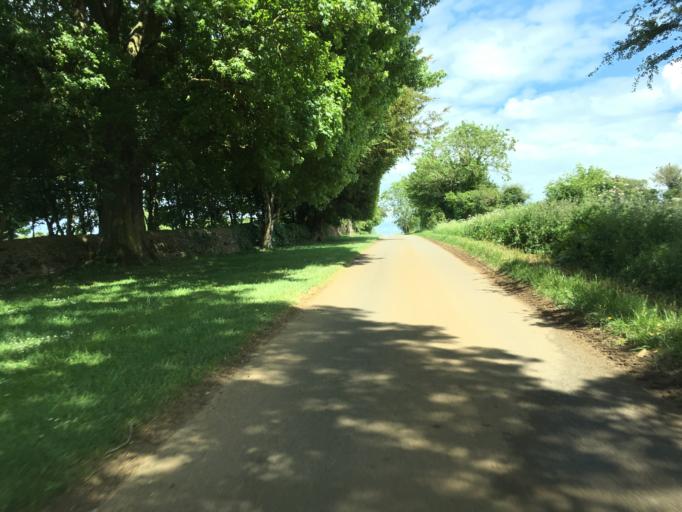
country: GB
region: England
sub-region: Gloucestershire
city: Coates
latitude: 51.6782
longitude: -2.0937
